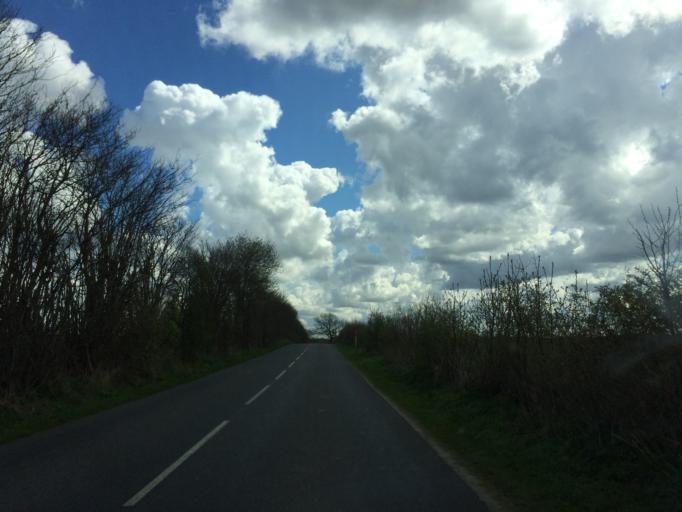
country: DK
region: South Denmark
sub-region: Assens Kommune
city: Tommerup
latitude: 55.2539
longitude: 10.2439
